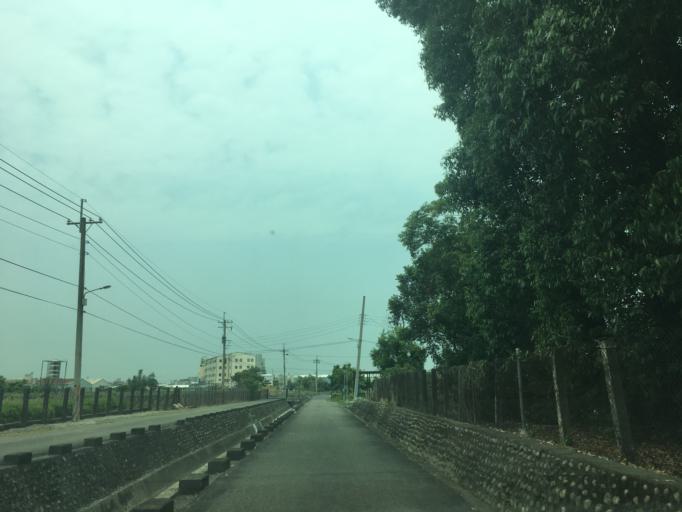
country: TW
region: Taiwan
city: Zhongxing New Village
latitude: 24.0338
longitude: 120.6891
